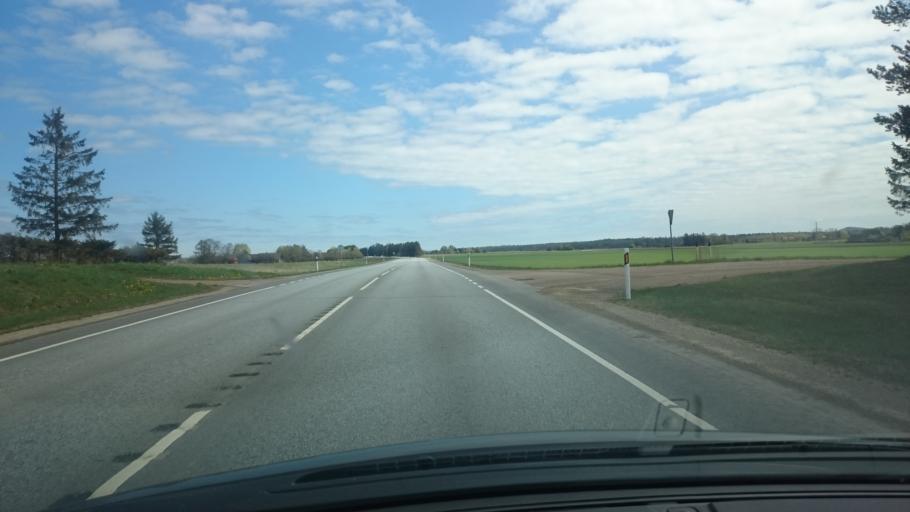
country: EE
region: Ida-Virumaa
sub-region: Kohtla-Nomme vald
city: Kohtla-Nomme
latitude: 59.4095
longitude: 27.1195
